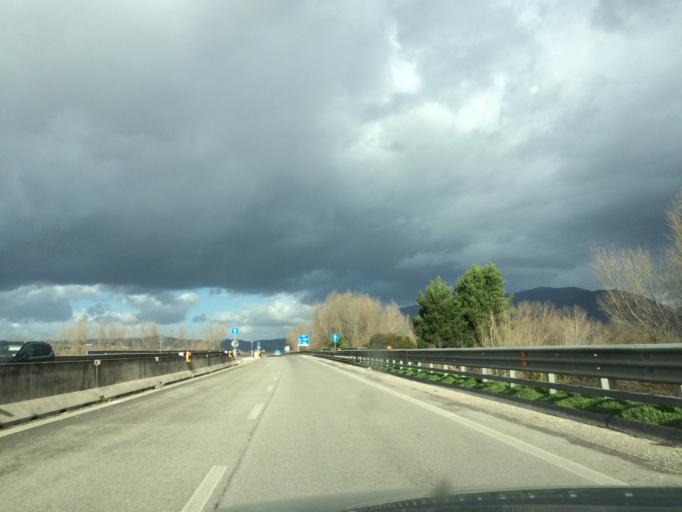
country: IT
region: Umbria
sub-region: Provincia di Terni
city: Terni
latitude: 42.5557
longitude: 12.5836
